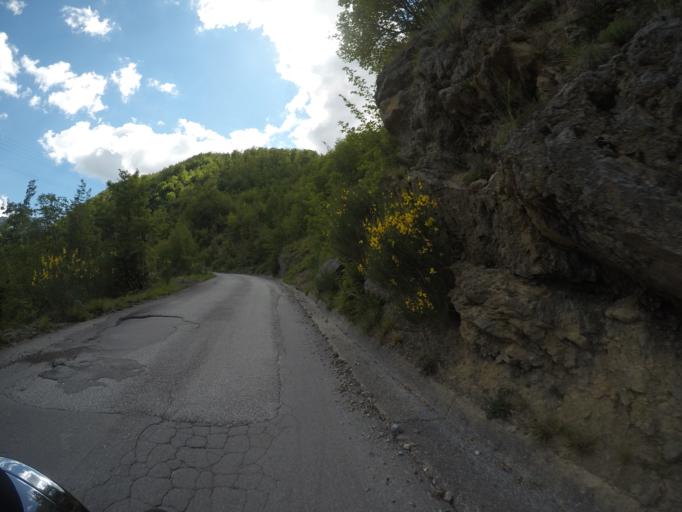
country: IT
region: Tuscany
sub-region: Provincia di Lucca
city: Minucciano
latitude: 44.1597
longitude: 10.2011
